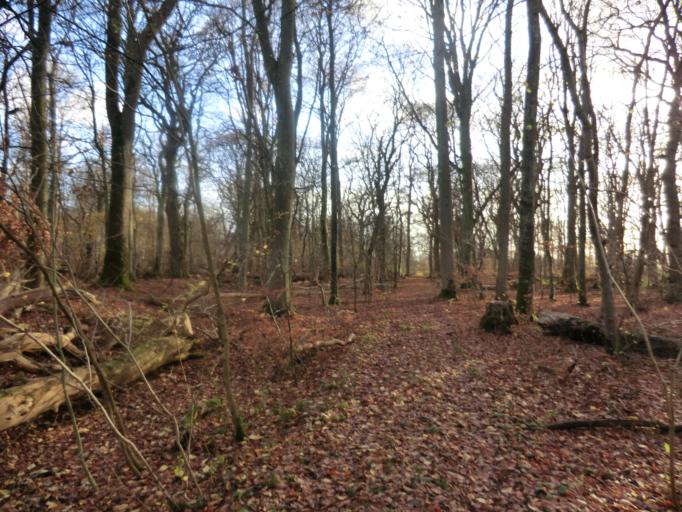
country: SE
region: Skane
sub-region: Lunds Kommun
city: Genarp
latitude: 55.6753
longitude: 13.3294
